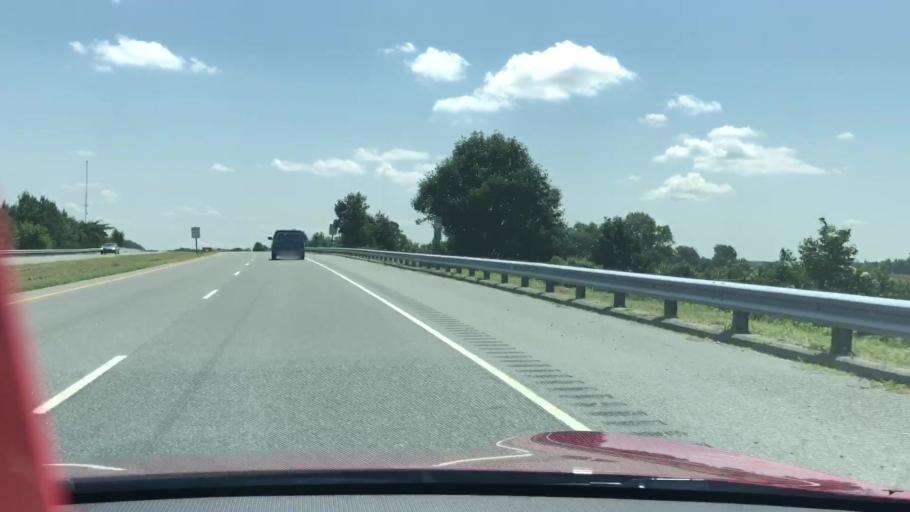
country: US
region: North Carolina
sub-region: Currituck County
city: Moyock
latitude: 36.6191
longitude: -76.2131
